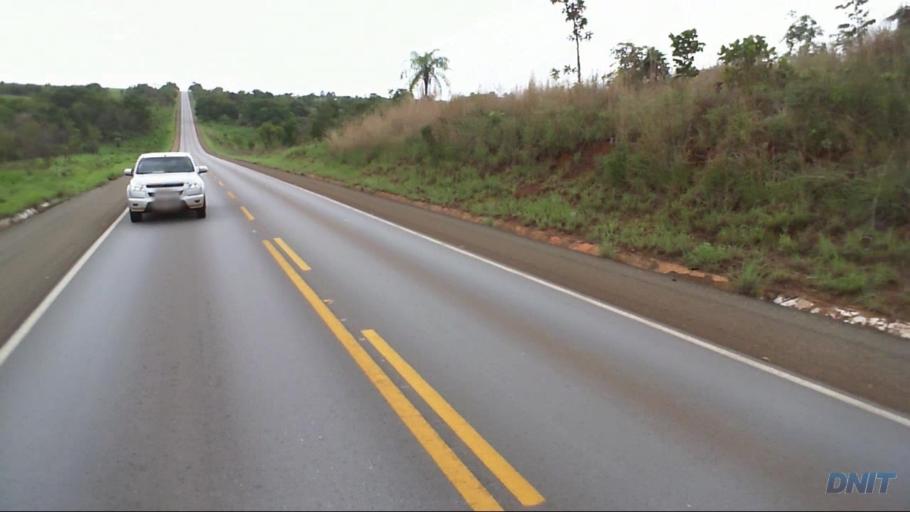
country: BR
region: Goias
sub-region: Barro Alto
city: Barro Alto
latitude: -14.8099
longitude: -49.0444
